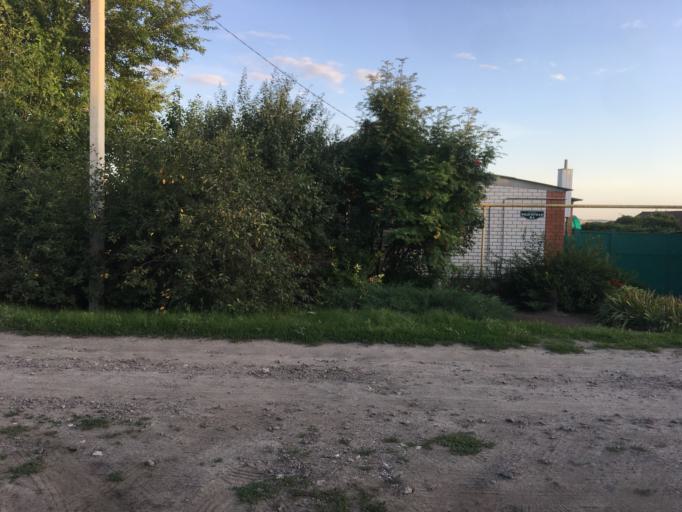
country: RU
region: Voronezj
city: Rossosh'
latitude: 50.2119
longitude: 39.5278
